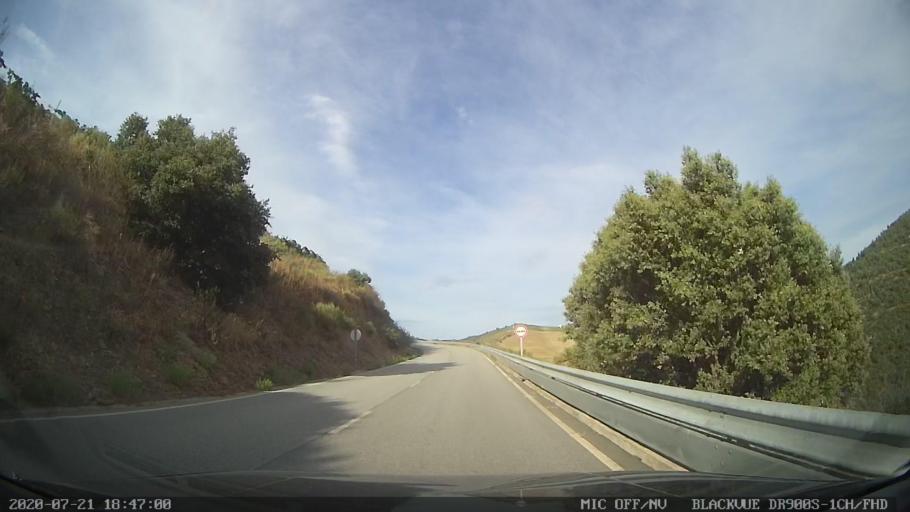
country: PT
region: Viseu
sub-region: Sao Joao da Pesqueira
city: Sao Joao da Pesqueira
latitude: 41.1185
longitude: -7.4414
